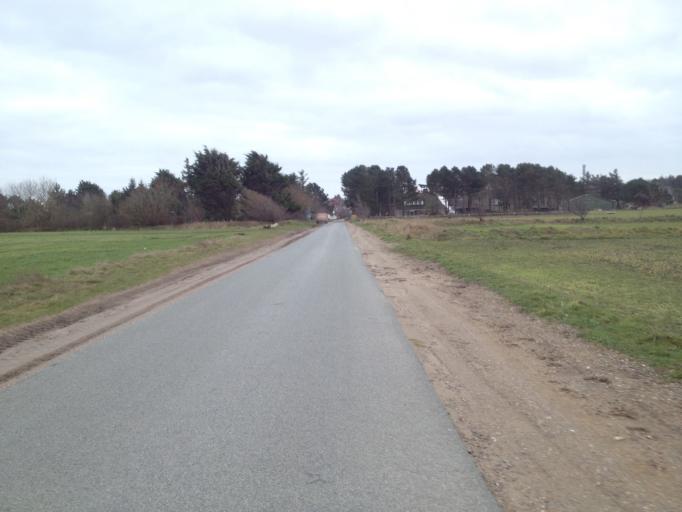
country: DE
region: Schleswig-Holstein
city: Nebel
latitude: 54.6571
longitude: 8.3511
